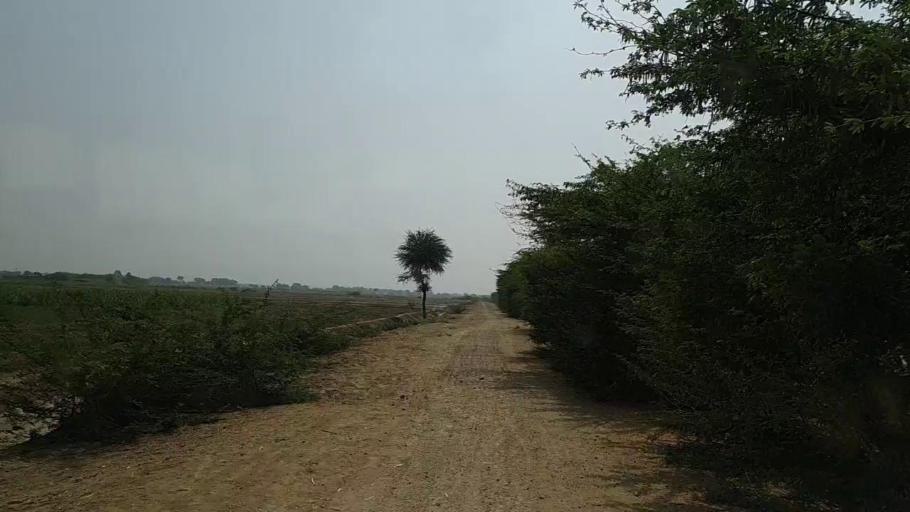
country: PK
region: Sindh
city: Naukot
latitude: 24.8121
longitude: 69.3614
